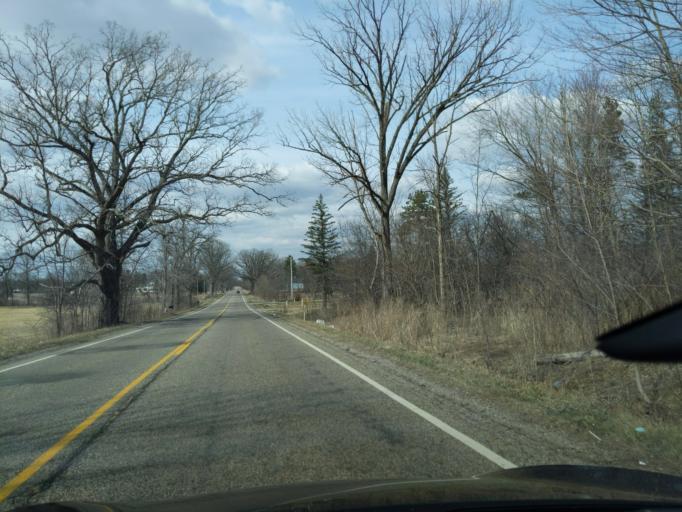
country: US
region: Michigan
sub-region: Jackson County
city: Jackson
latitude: 42.3296
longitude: -84.4136
